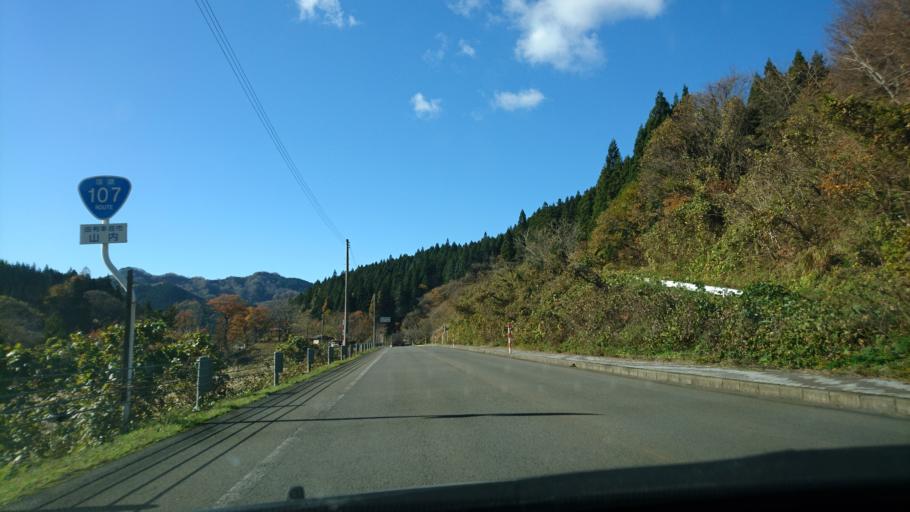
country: JP
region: Akita
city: Omagari
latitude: 39.3249
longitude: 140.1882
